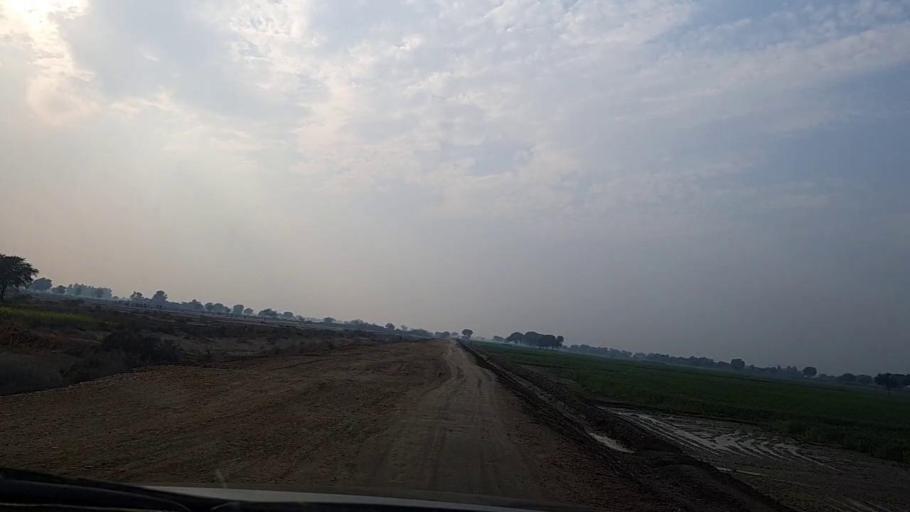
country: PK
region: Sindh
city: Nawabshah
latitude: 26.2737
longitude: 68.3393
